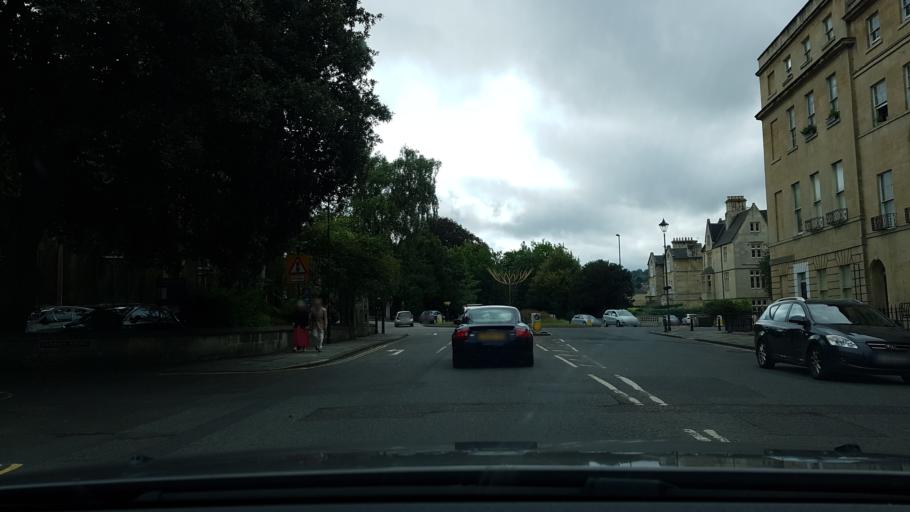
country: GB
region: England
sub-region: Bath and North East Somerset
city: Bath
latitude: 51.3847
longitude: -2.3514
